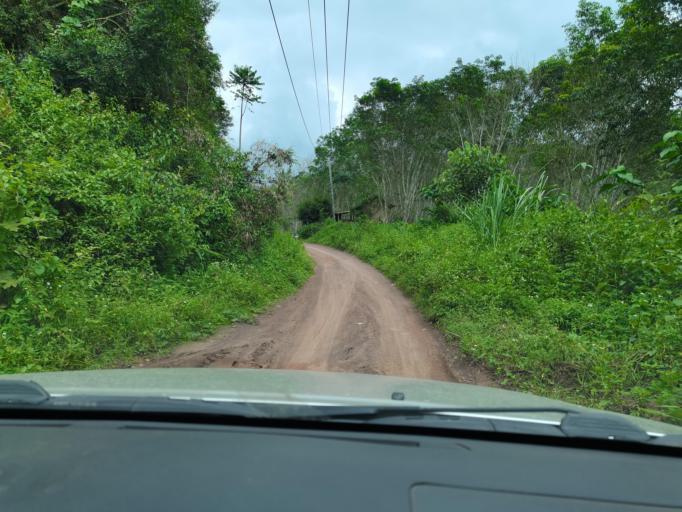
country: LA
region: Loungnamtha
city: Muang Long
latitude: 20.7012
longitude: 101.0288
